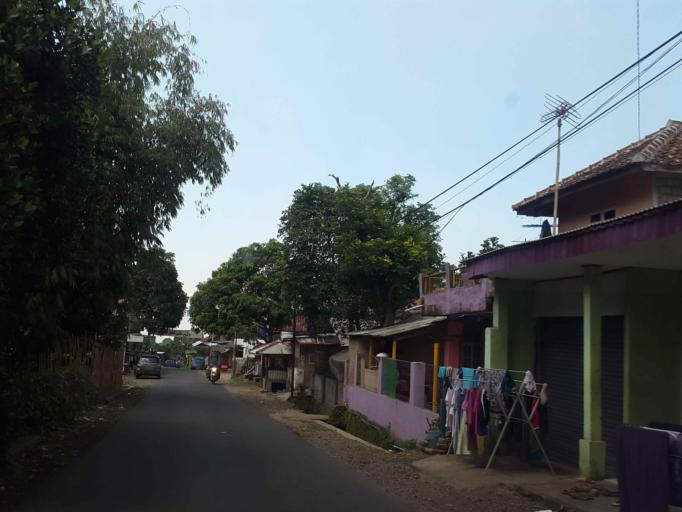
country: ID
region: West Java
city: Ciranjang-hilir
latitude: -6.7983
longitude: 107.0770
